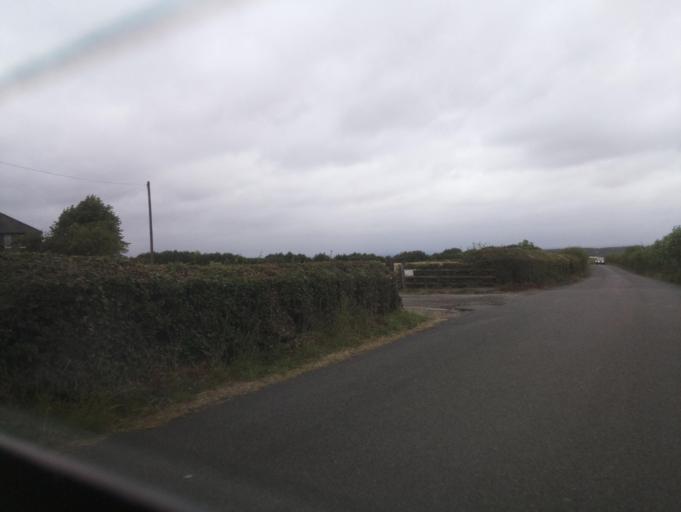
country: GB
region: England
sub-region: Leicestershire
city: Ashby de la Zouch
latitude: 52.7740
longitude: -1.5055
